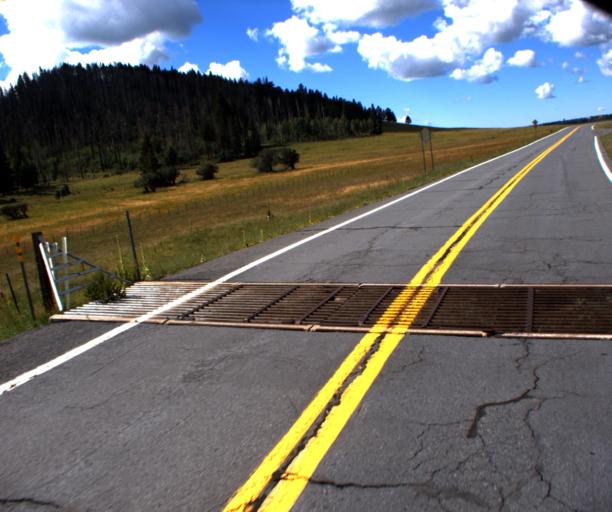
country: US
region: Arizona
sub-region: Apache County
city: Eagar
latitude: 33.9148
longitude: -109.4120
